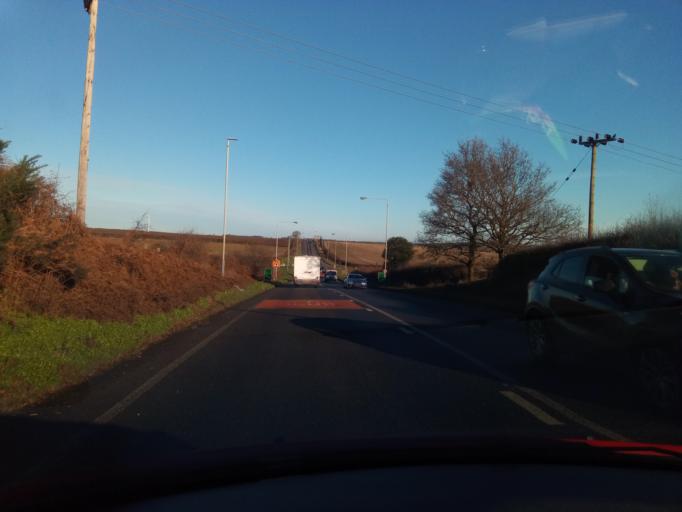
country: GB
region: England
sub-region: Nottinghamshire
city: Farnsfield
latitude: 53.0931
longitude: -1.0690
